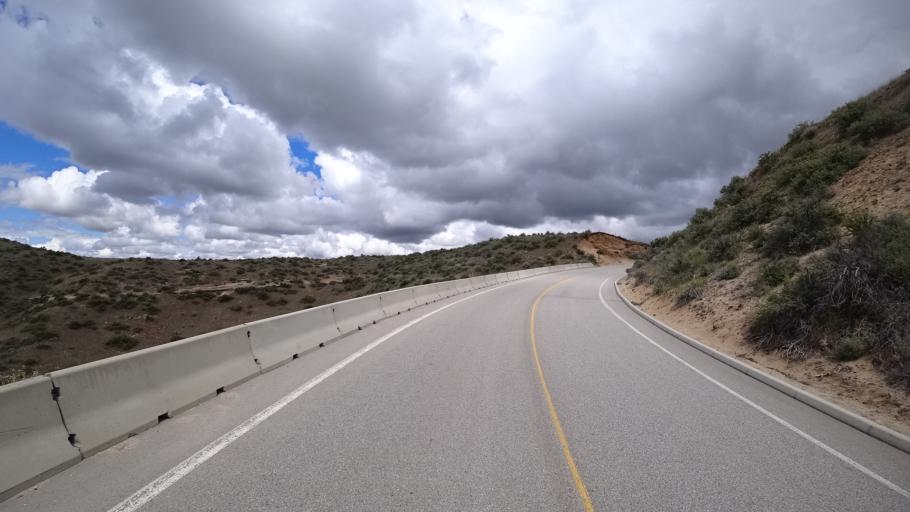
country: US
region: Idaho
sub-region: Ada County
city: Boise
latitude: 43.6911
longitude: -116.1837
